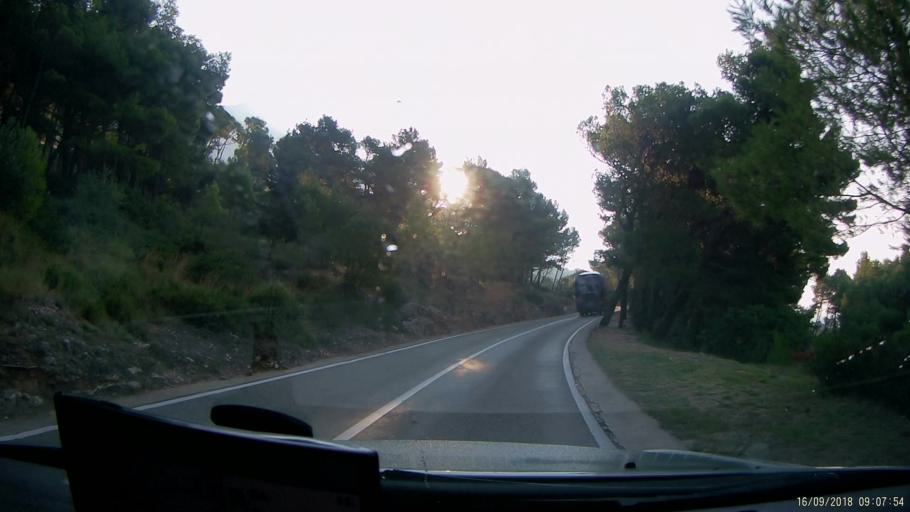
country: HR
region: Splitsko-Dalmatinska
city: Donja Brela
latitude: 43.3723
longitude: 16.9280
